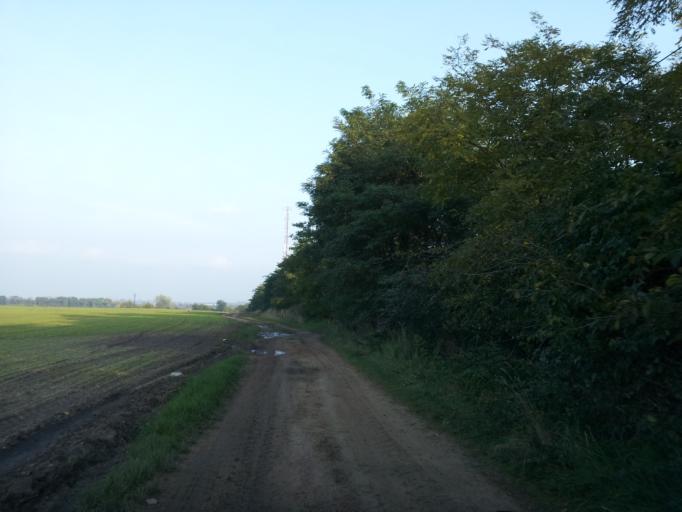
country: HU
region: Komarom-Esztergom
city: Kisber
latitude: 47.5123
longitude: 18.0145
